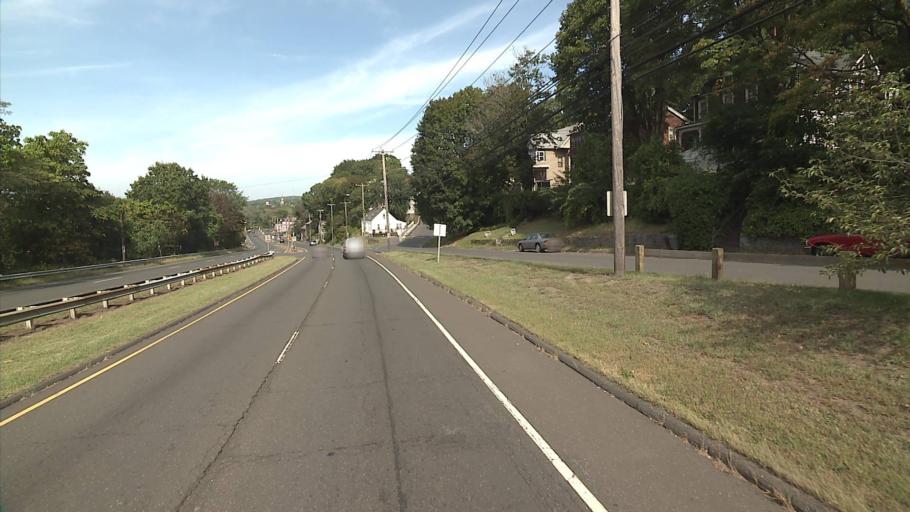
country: US
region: Connecticut
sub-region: New Haven County
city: Derby
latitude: 41.3129
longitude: -73.0770
